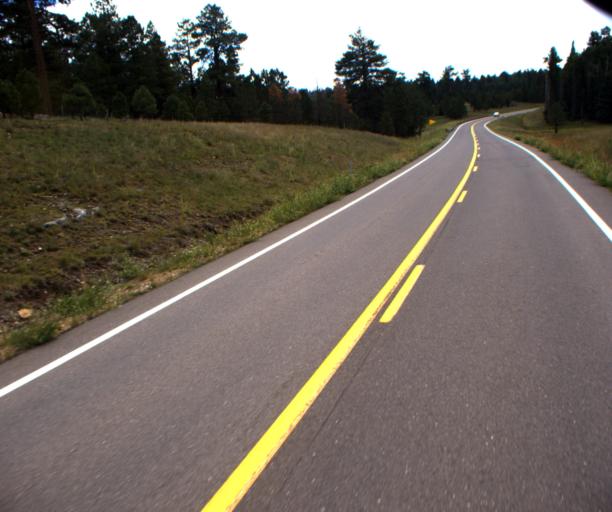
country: US
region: Arizona
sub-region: Apache County
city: Eagar
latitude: 33.9845
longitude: -109.5069
